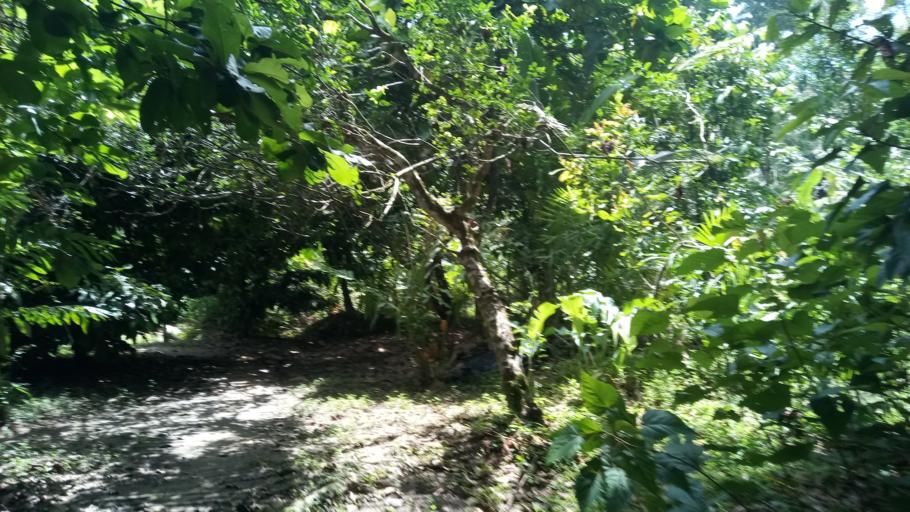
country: CR
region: Limon
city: Sixaola
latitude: 9.6235
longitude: -82.6213
